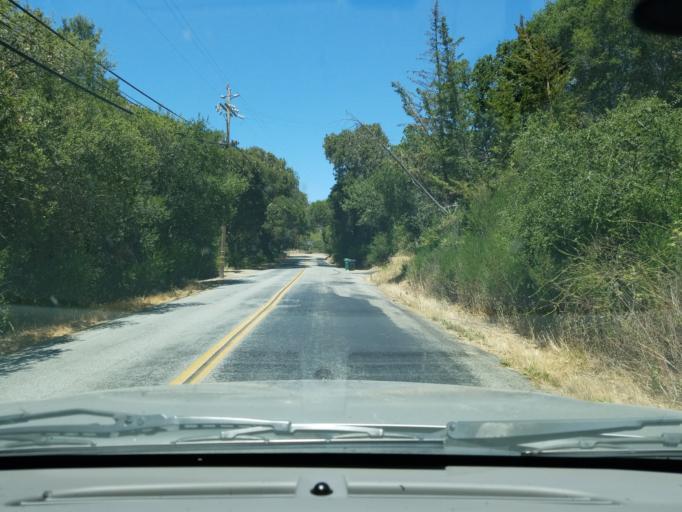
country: US
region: California
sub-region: Monterey County
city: Carmel Valley Village
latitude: 36.4595
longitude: -121.7079
